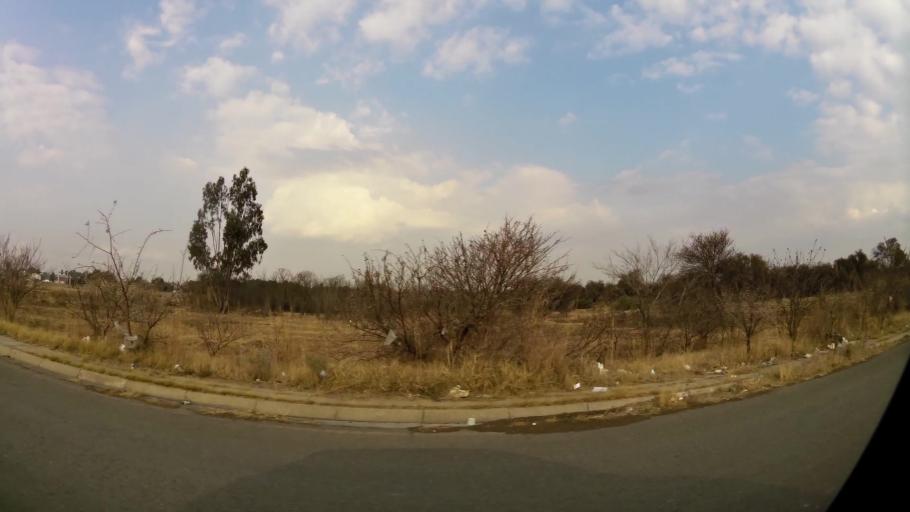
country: ZA
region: Gauteng
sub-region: Sedibeng District Municipality
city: Vereeniging
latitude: -26.6872
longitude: 27.9019
